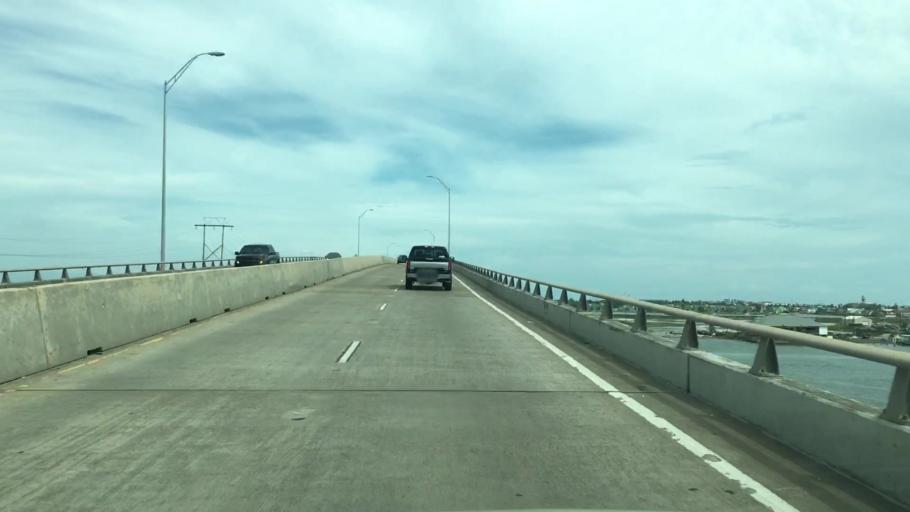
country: US
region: Texas
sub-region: Nueces County
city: Corpus Christi
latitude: 27.6360
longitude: -97.2427
